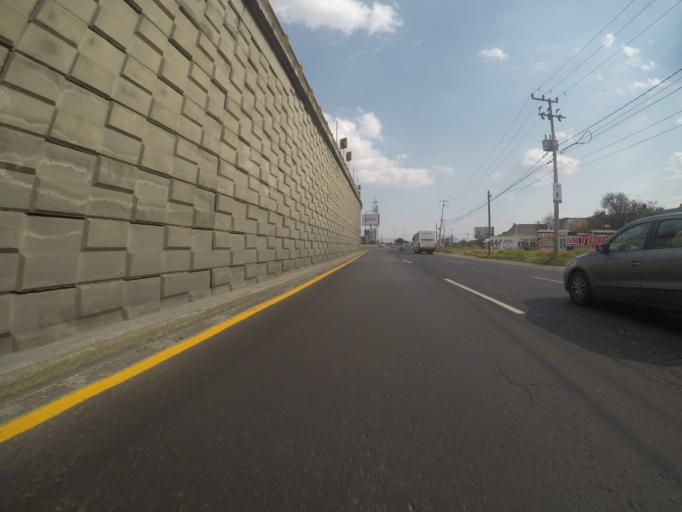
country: MX
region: Mexico
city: San Mateo Mexicaltzingo
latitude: 19.2172
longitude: -99.5914
